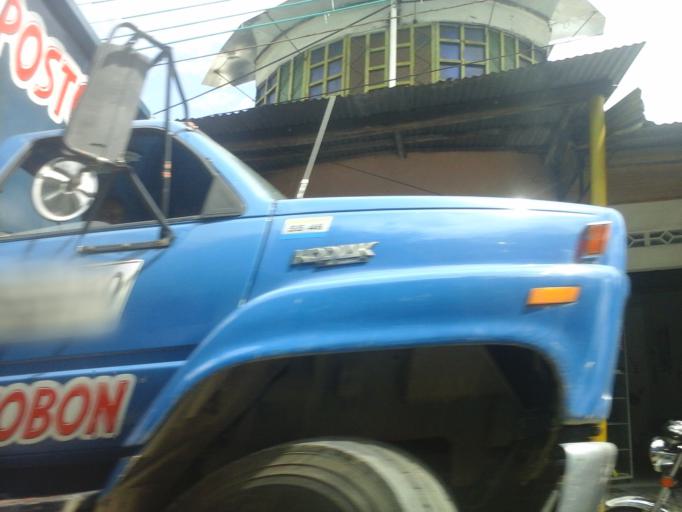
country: CO
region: Caqueta
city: El Paujil
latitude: 1.5697
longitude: -75.3265
